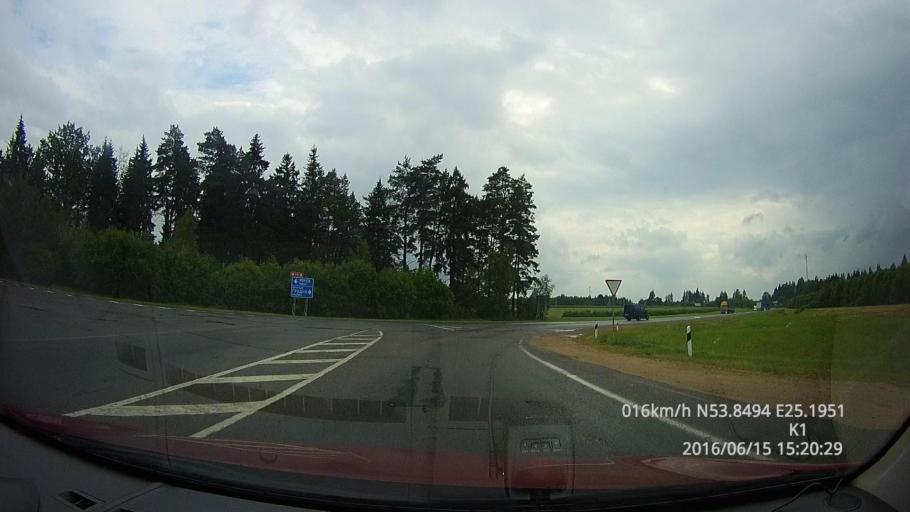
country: BY
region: Grodnenskaya
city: Lida
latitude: 53.8492
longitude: 25.1952
